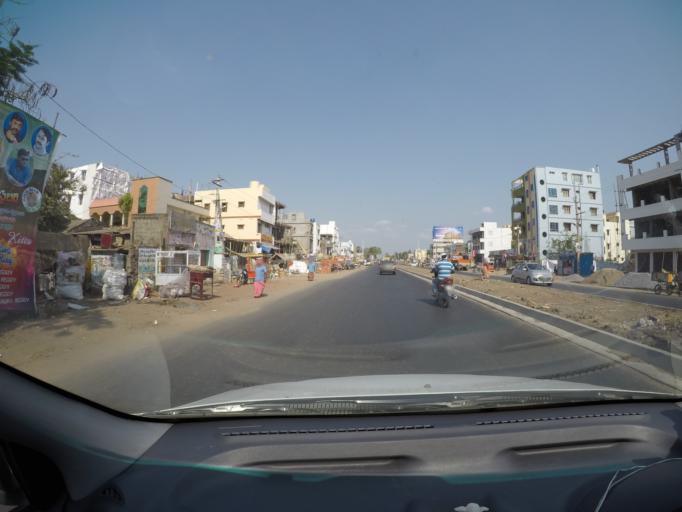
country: IN
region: Andhra Pradesh
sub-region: Krishna
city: Yanamalakuduru
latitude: 16.4769
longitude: 80.7052
